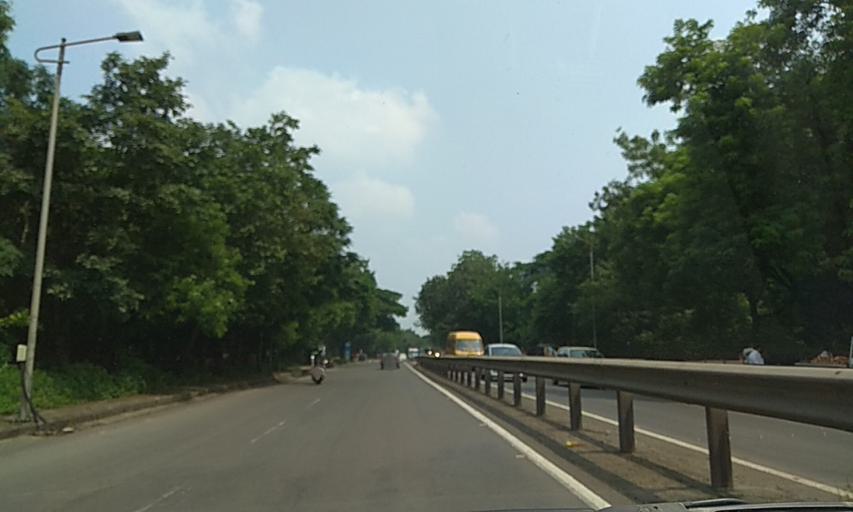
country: IN
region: Maharashtra
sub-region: Pune Division
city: Shivaji Nagar
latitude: 18.5393
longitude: 73.8105
